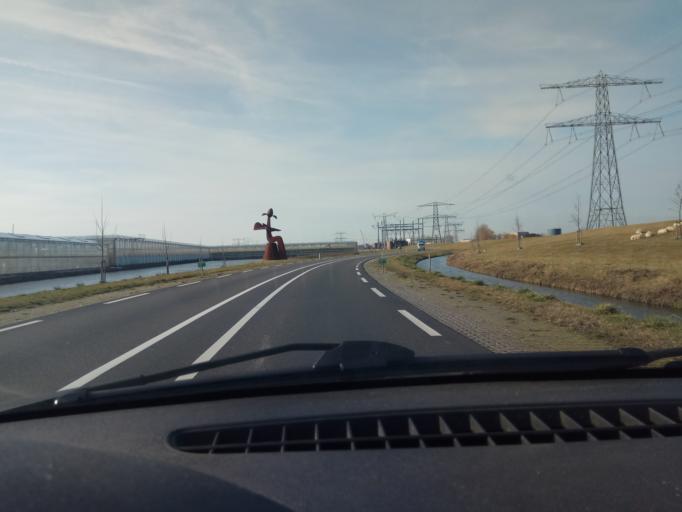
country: NL
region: South Holland
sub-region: Gemeente Westland
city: De Lier
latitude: 51.9845
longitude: 4.2321
